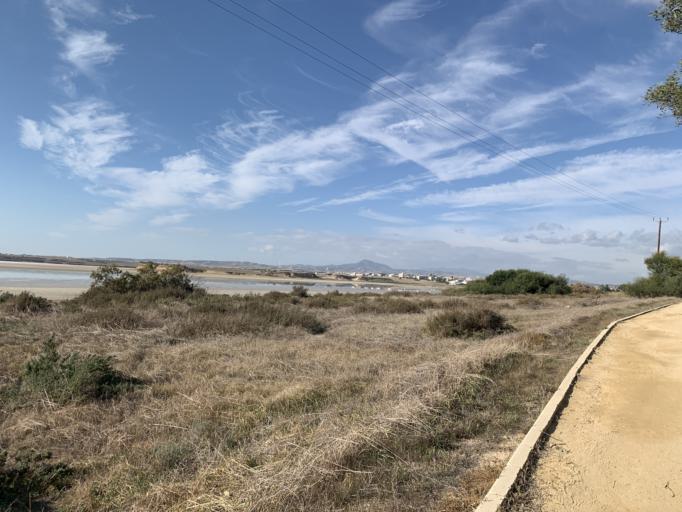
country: CY
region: Larnaka
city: Larnaca
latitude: 34.9080
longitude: 33.6157
